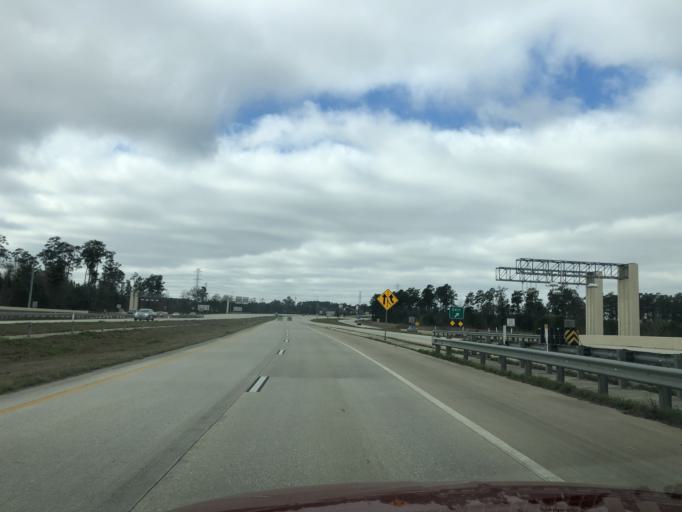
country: US
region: Texas
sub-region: Harris County
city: Spring
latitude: 30.0913
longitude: -95.4420
